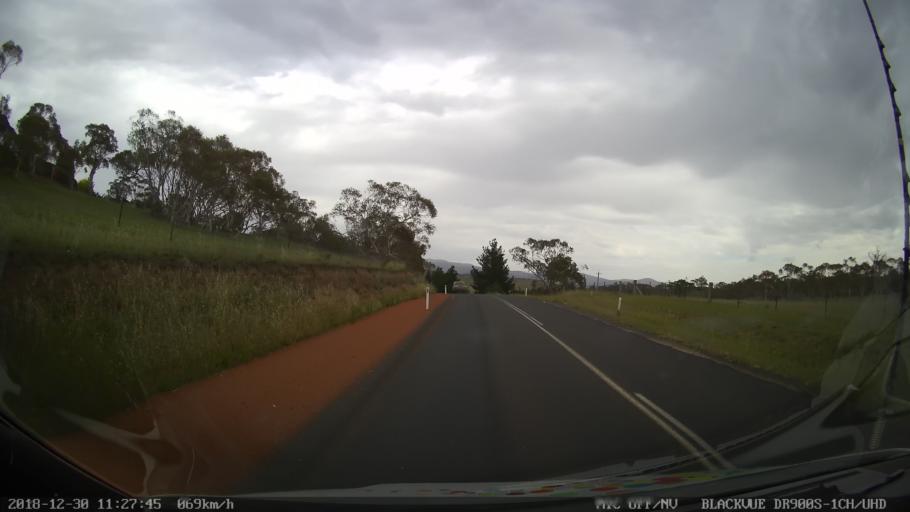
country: AU
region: New South Wales
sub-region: Snowy River
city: Jindabyne
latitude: -36.4578
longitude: 148.6244
